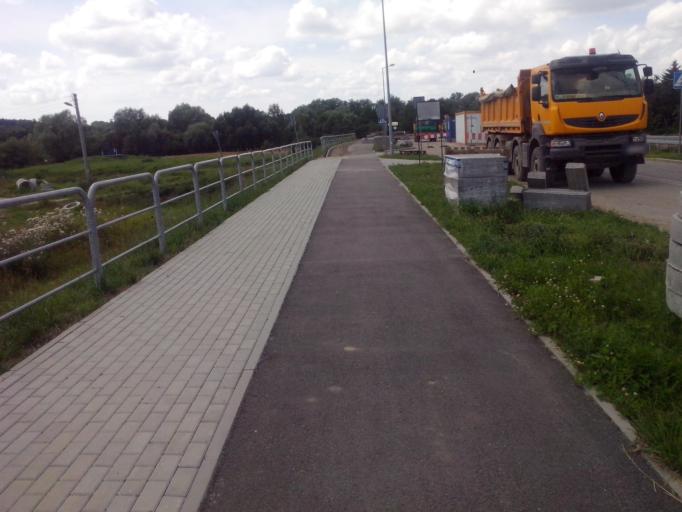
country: PL
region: Subcarpathian Voivodeship
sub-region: Powiat strzyzowski
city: Strzyzow
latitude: 49.8662
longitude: 21.7847
